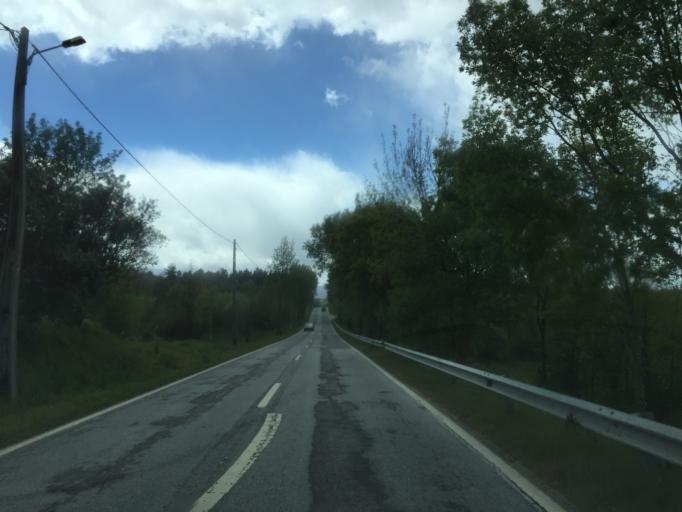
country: PT
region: Guarda
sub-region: Celorico da Beira
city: Celorico da Beira
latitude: 40.5826
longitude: -7.4507
